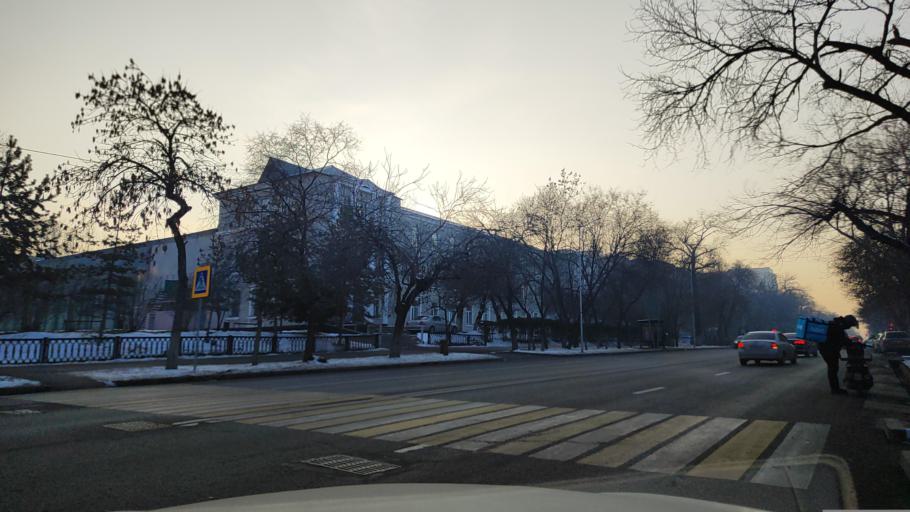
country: KZ
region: Almaty Qalasy
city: Almaty
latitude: 43.2559
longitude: 76.9602
